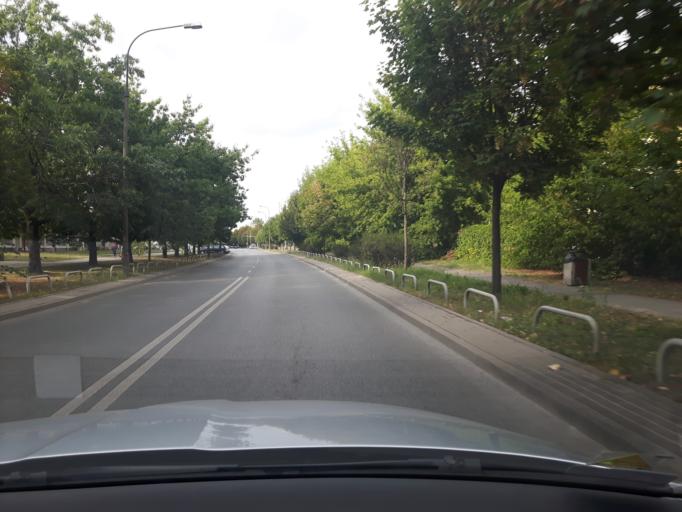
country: PL
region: Masovian Voivodeship
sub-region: Warszawa
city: Mokotow
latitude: 52.1776
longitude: 21.0138
